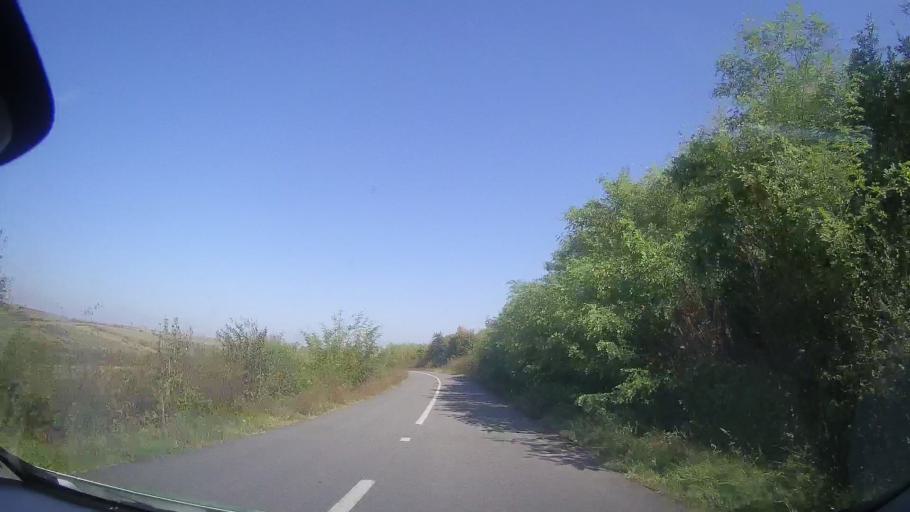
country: RO
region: Timis
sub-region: Comuna Balint
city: Balint
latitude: 45.8313
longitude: 21.8550
